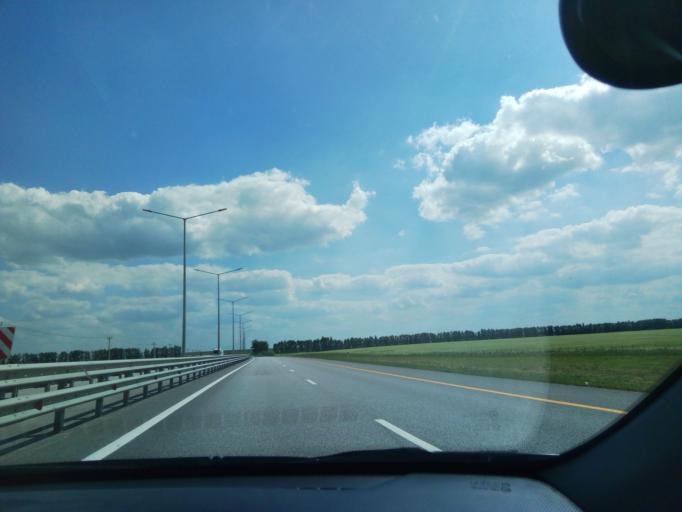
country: RU
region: Voronezj
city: Podkletnoye
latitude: 51.5221
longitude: 39.5107
